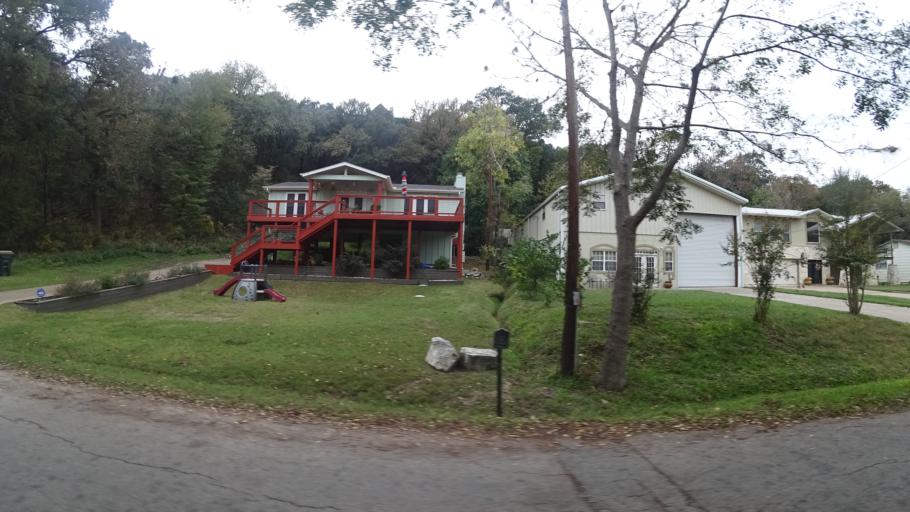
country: US
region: Texas
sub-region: Travis County
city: Hudson Bend
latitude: 30.3763
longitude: -97.9174
